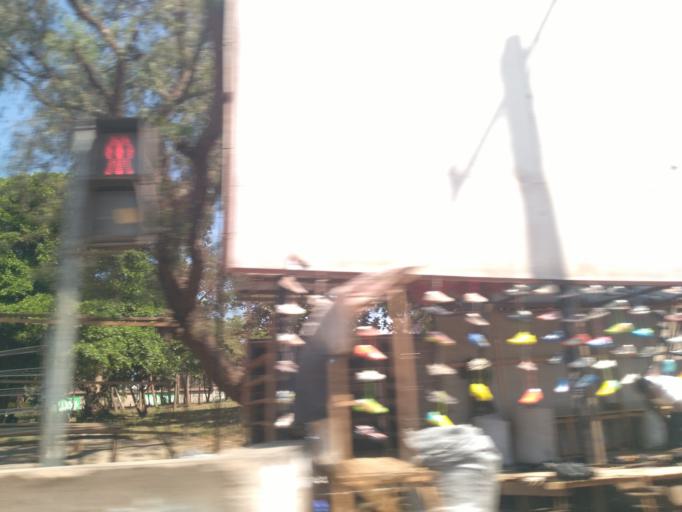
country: TZ
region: Arusha
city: Arusha
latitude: -3.3701
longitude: 36.6848
